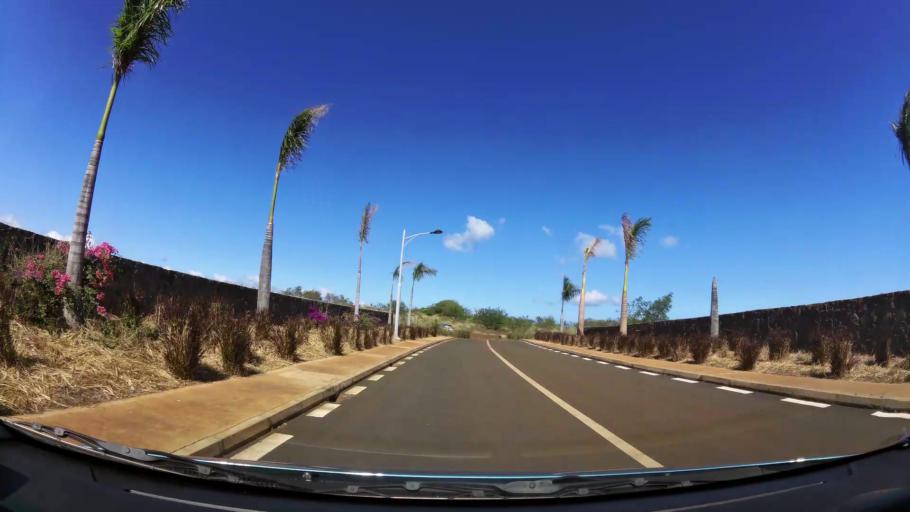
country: MU
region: Black River
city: Flic en Flac
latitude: -20.2704
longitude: 57.3817
